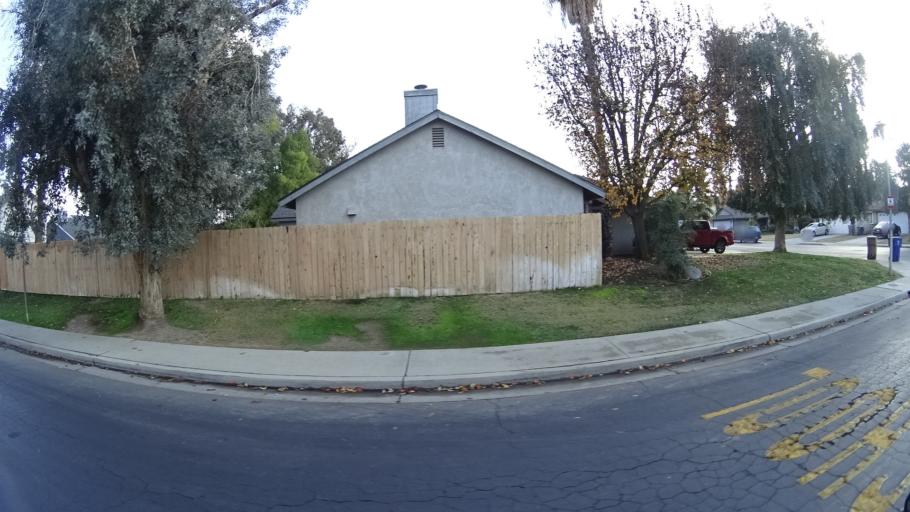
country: US
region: California
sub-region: Kern County
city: Greenacres
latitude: 35.3139
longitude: -119.1049
